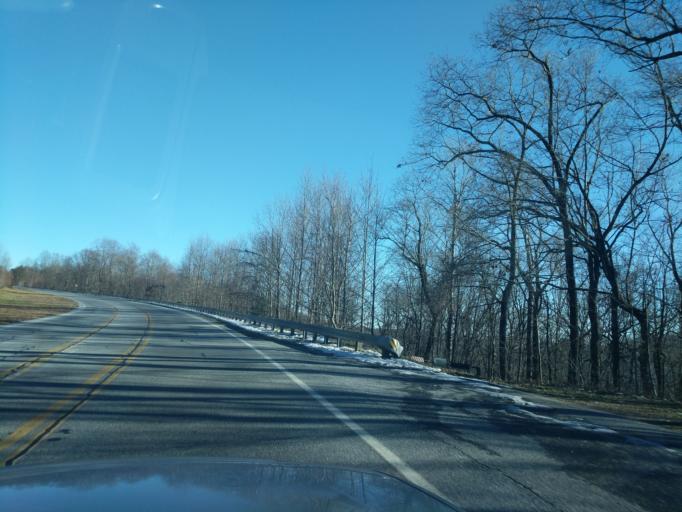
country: US
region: Georgia
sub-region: Towns County
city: Hiawassee
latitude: 34.8938
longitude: -83.6009
